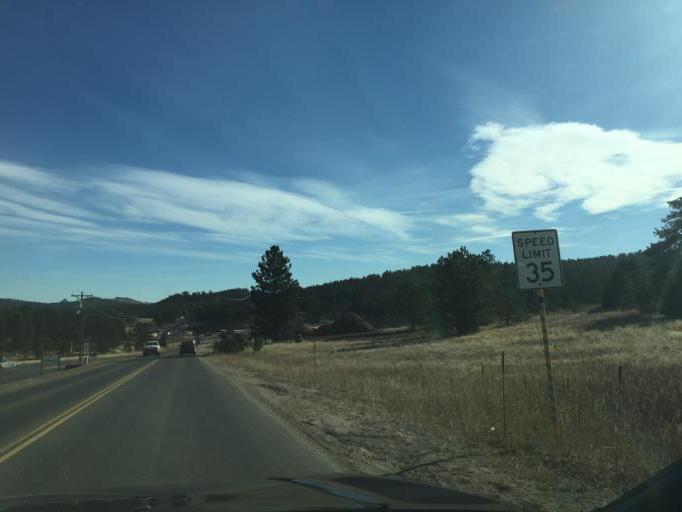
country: US
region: Colorado
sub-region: Jefferson County
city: Evergreen
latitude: 39.4416
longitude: -105.4578
